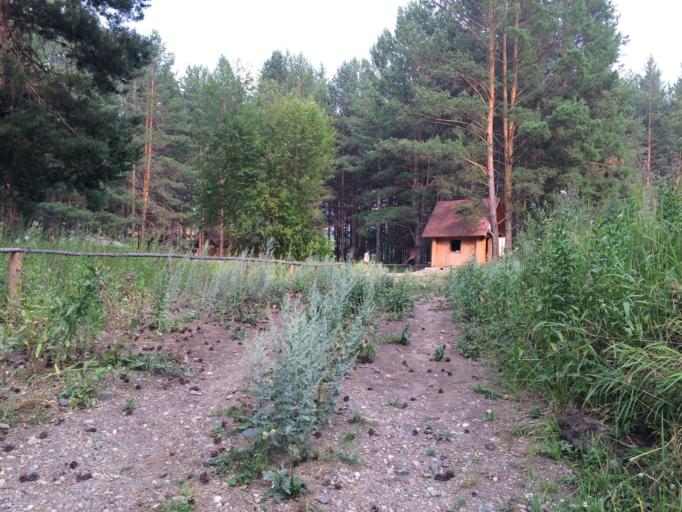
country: RU
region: Bashkortostan
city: Abzakovo
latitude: 53.7954
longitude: 58.6288
